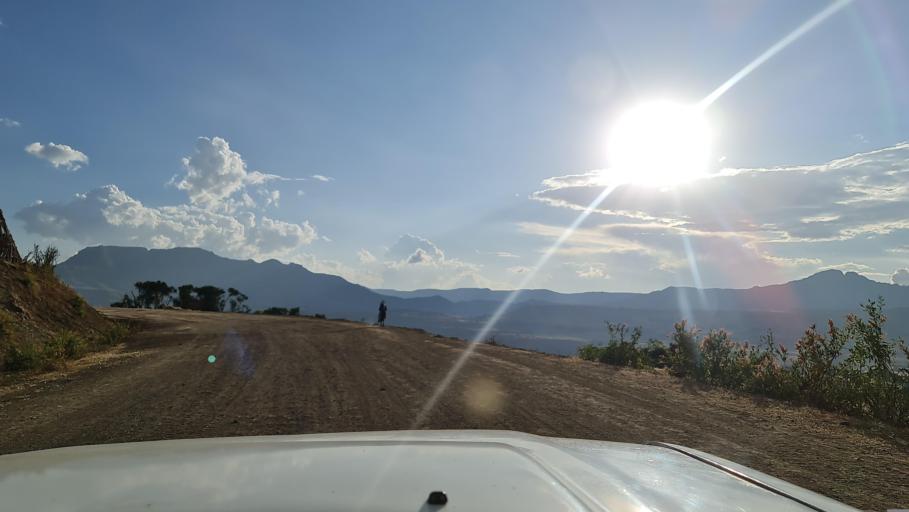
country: ET
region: Amhara
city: Debark'
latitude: 13.0569
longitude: 38.0182
